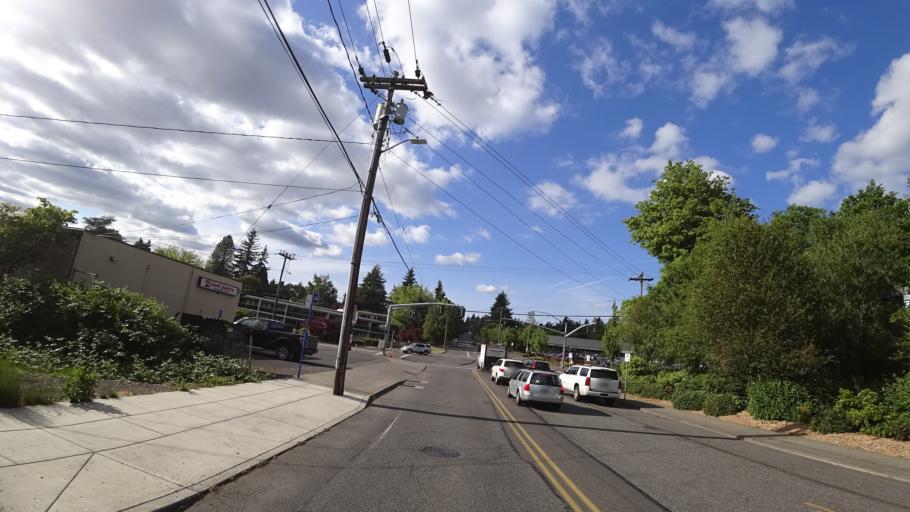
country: US
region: Oregon
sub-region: Washington County
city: Garden Home-Whitford
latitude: 45.4758
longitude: -122.7232
